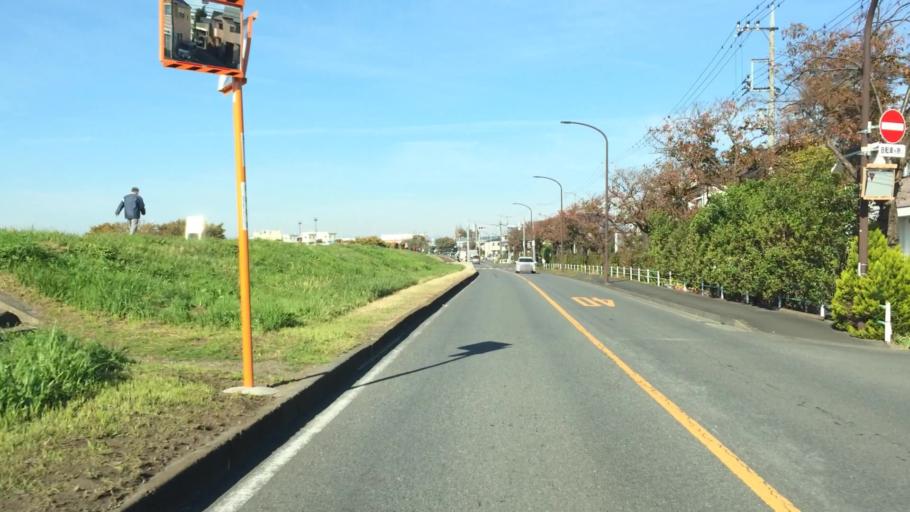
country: JP
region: Tokyo
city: Chofugaoka
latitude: 35.6521
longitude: 139.5174
